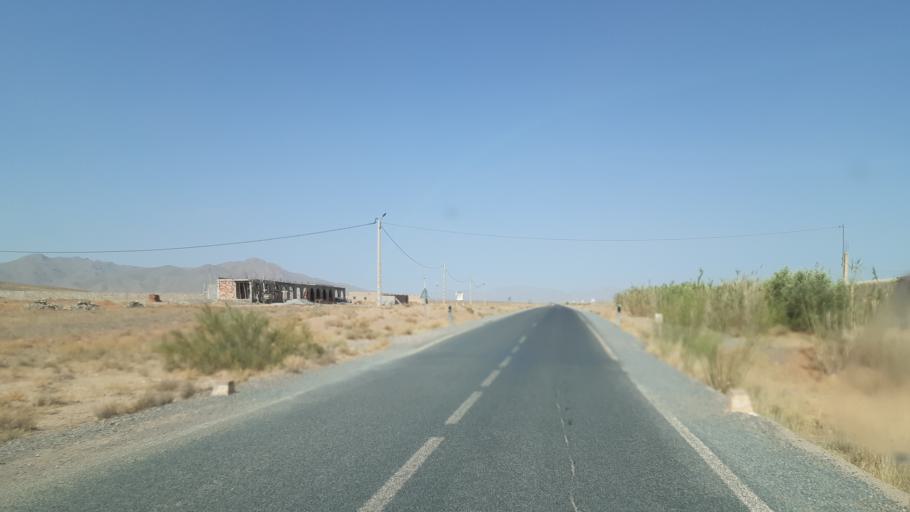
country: MA
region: Meknes-Tafilalet
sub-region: Errachidia
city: Amouguer
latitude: 32.2373
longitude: -4.6191
